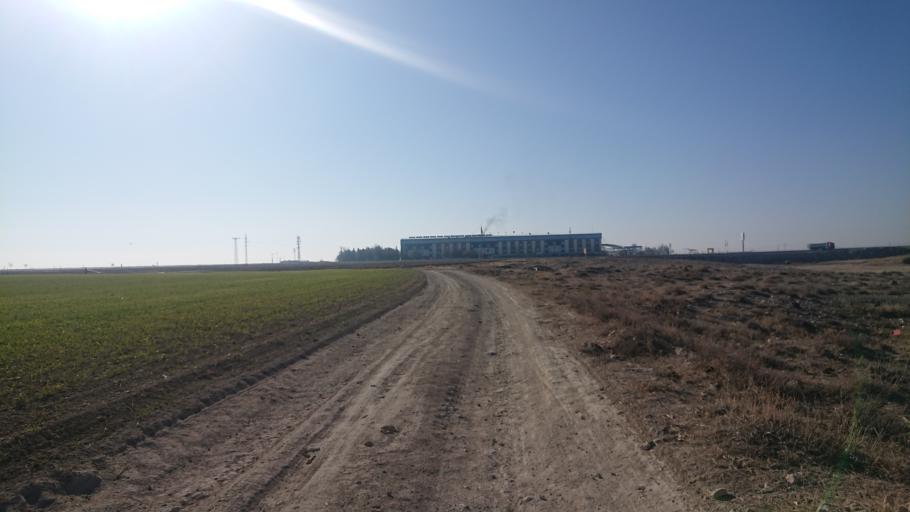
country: TR
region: Aksaray
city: Sultanhani
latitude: 38.2549
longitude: 33.5085
